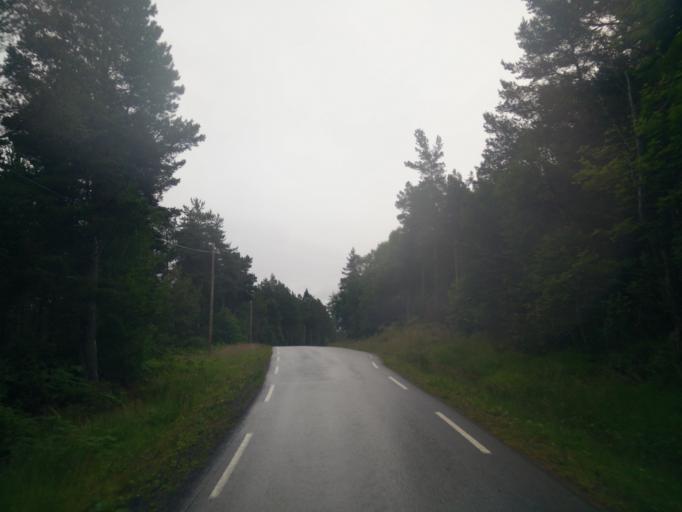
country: NO
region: More og Romsdal
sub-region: Kristiansund
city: Rensvik
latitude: 63.0249
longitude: 7.8991
